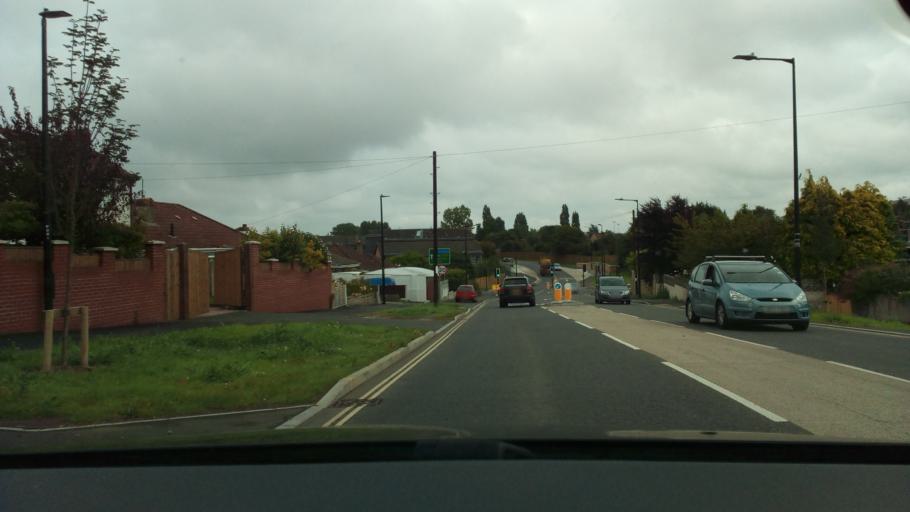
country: GB
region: England
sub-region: North Somerset
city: Dundry
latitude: 51.4112
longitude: -2.6213
